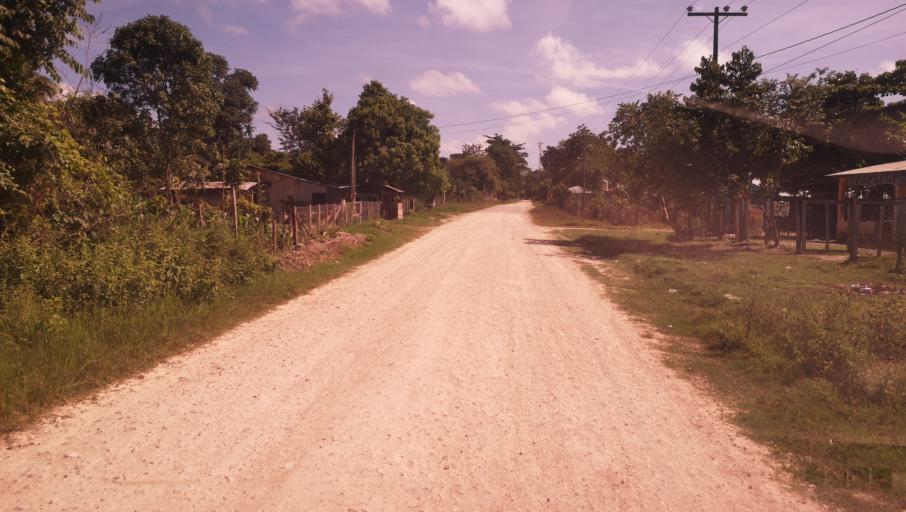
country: GT
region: Peten
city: Melchor de Mencos
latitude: 16.8371
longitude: -89.3002
